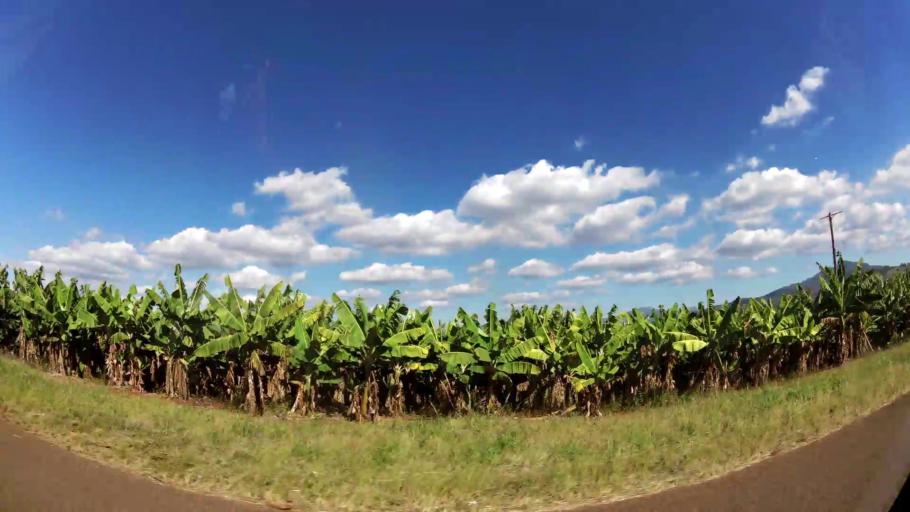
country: ZA
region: Limpopo
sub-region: Mopani District Municipality
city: Tzaneen
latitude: -23.8030
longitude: 30.1183
